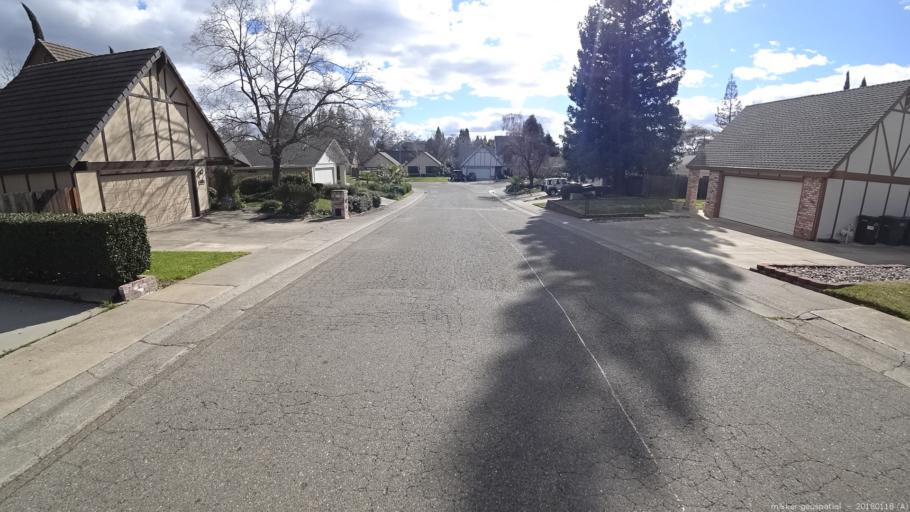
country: US
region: California
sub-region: Sacramento County
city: Orangevale
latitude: 38.6746
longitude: -121.2111
